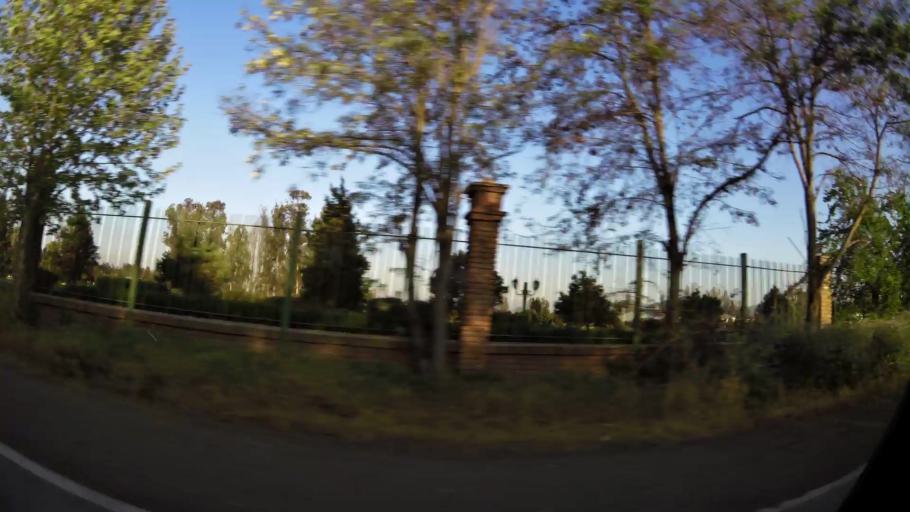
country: CL
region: Santiago Metropolitan
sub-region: Provincia de Talagante
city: Penaflor
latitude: -33.6072
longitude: -70.8482
